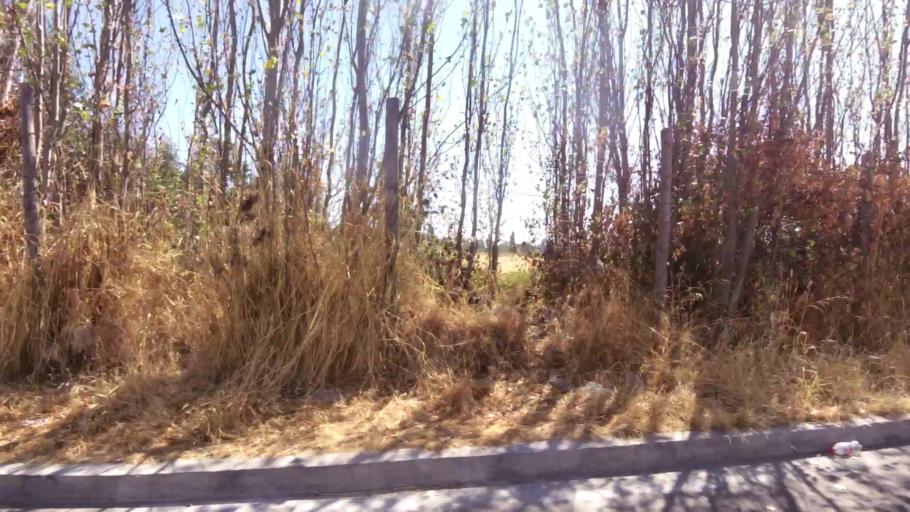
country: CL
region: Maule
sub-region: Provincia de Curico
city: Curico
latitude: -34.9602
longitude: -71.2323
